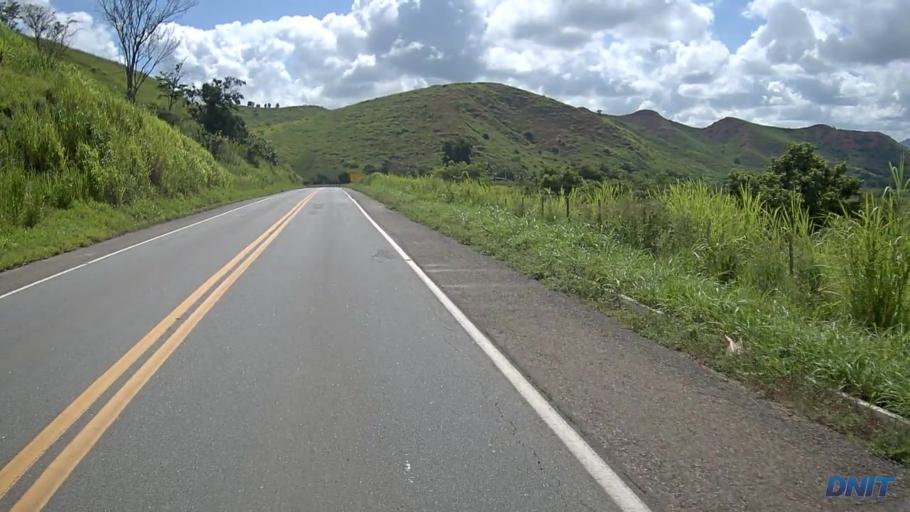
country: BR
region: Minas Gerais
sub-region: Belo Oriente
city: Belo Oriente
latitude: -19.1377
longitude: -42.2171
